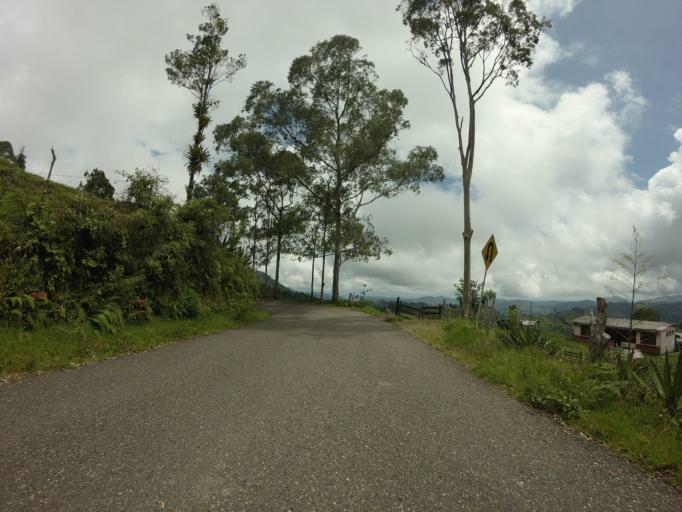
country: CO
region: Caldas
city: Manzanares
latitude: 5.2673
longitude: -75.1246
